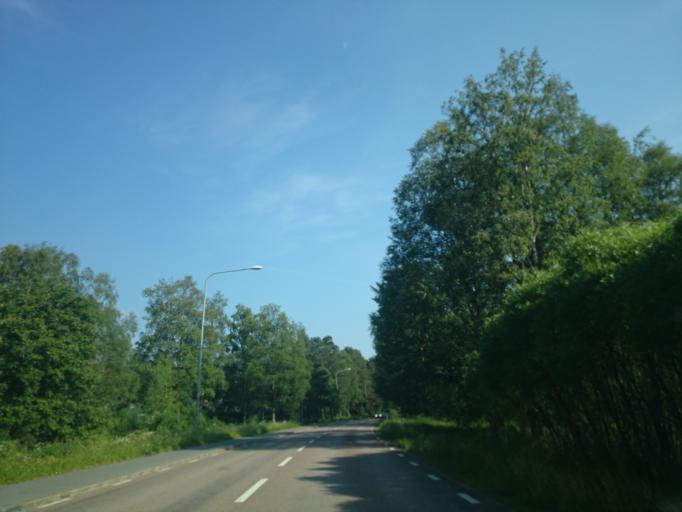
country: SE
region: Jaemtland
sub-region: OEstersunds Kommun
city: Brunflo
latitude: 62.9551
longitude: 15.0445
